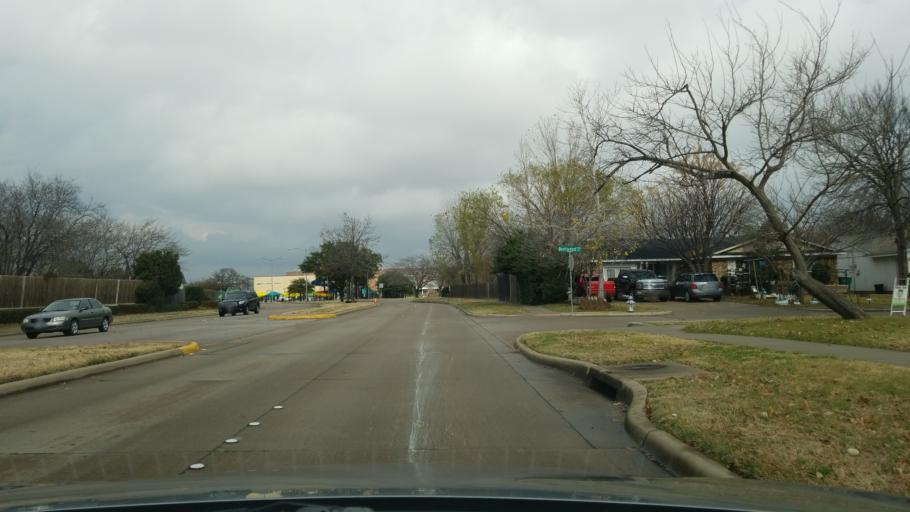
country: US
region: Texas
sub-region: Denton County
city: Lewisville
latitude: 33.0361
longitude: -97.0188
